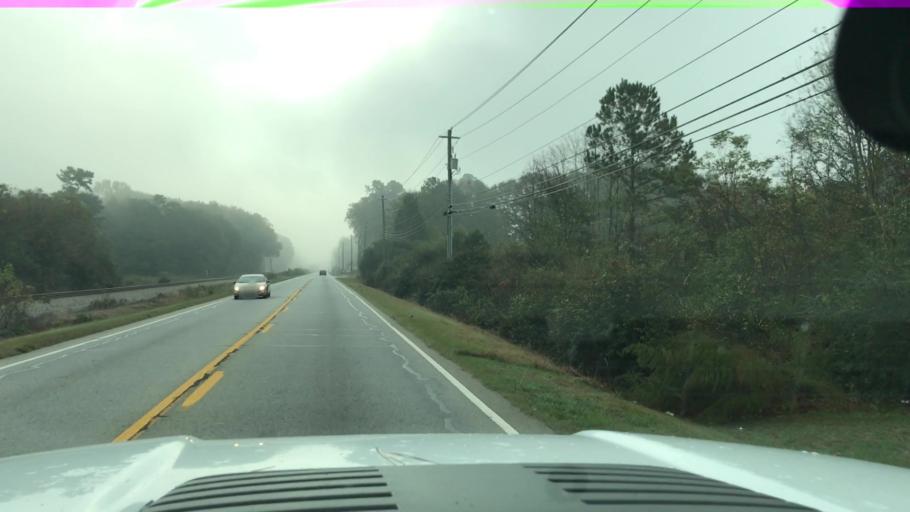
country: US
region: Georgia
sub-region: Barrow County
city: Russell
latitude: 33.9773
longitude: -83.7026
